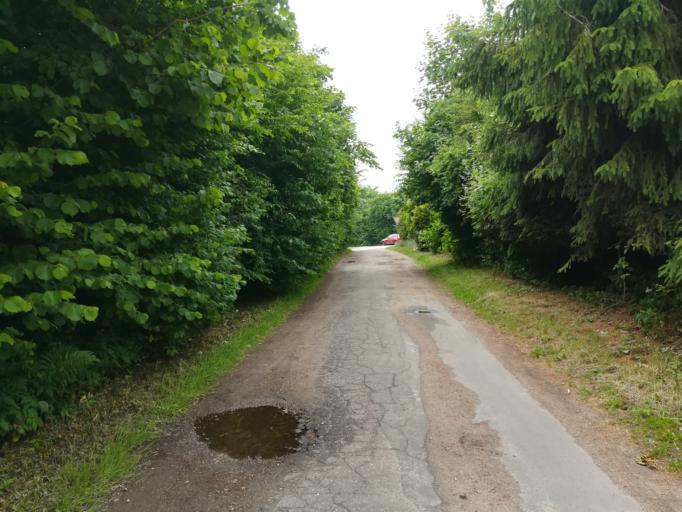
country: DE
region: Schleswig-Holstein
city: Stipsdorf
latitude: 53.9354
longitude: 10.3332
